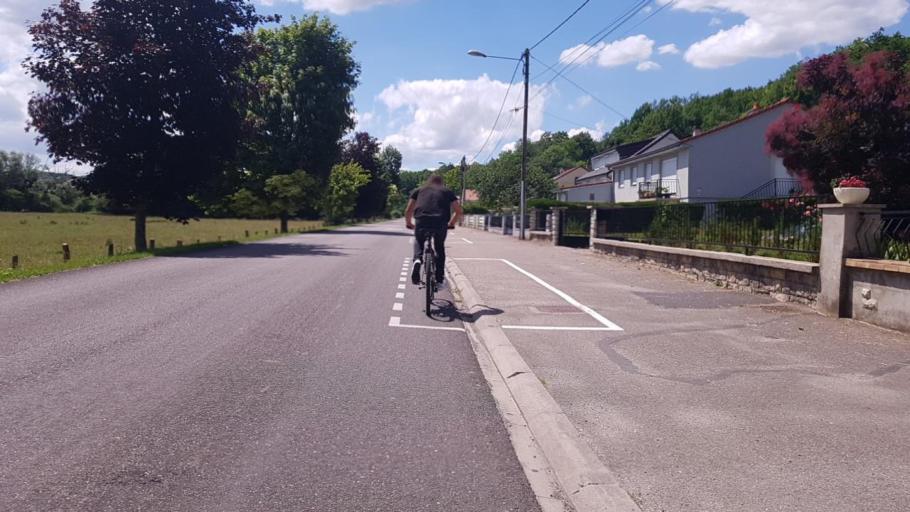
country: FR
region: Lorraine
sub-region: Departement de la Meuse
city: Vacon
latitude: 48.6792
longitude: 5.6105
